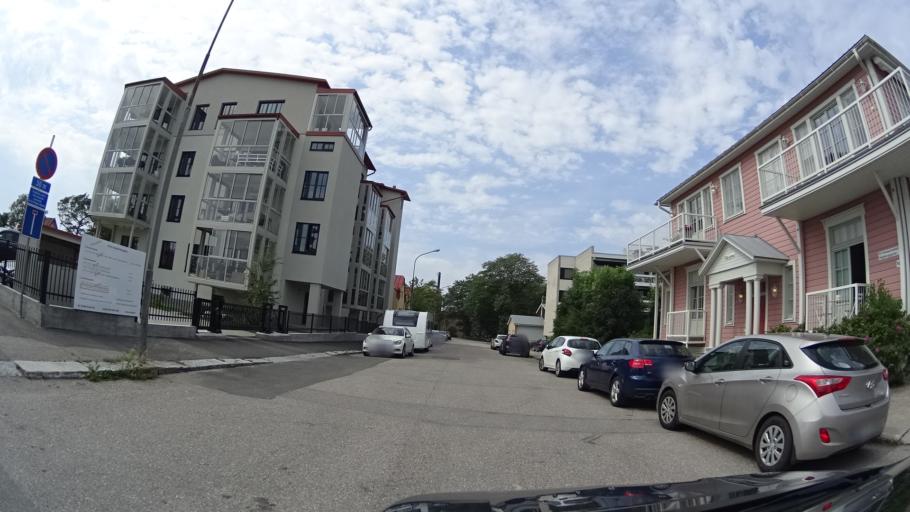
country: FI
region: Uusimaa
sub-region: Raaseporin
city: Hanko
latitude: 59.8227
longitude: 22.9649
